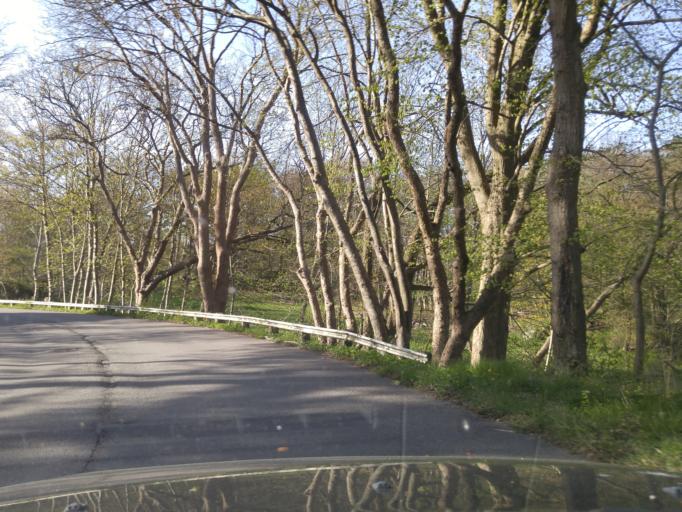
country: SE
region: Vaestra Goetaland
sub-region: Goteborg
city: Majorna
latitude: 57.6825
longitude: 11.9338
